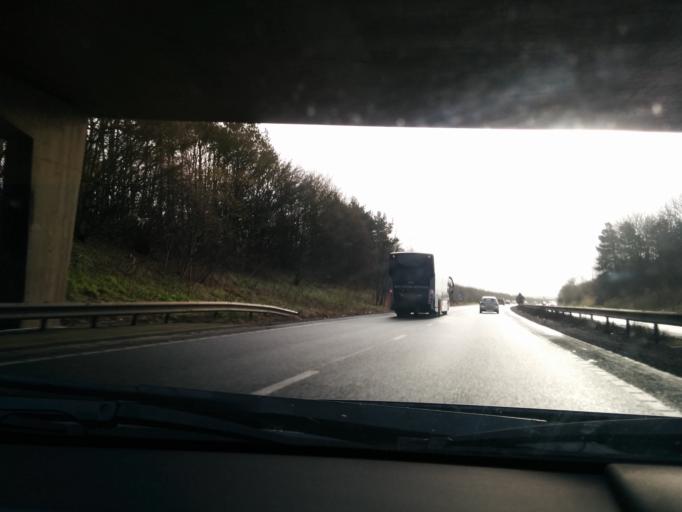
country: GB
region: England
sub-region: Oxfordshire
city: Harwell
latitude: 51.6015
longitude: -1.2797
